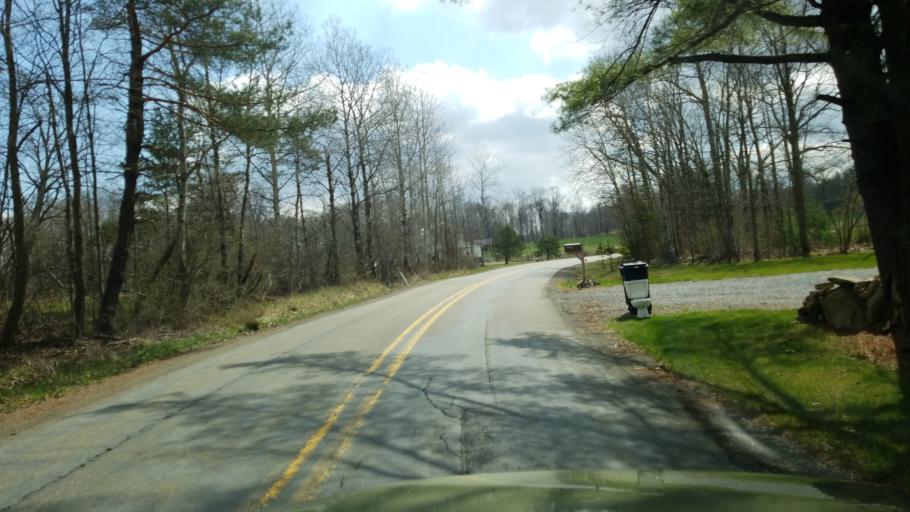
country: US
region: Pennsylvania
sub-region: Jefferson County
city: Brockway
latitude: 41.2785
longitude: -78.8440
